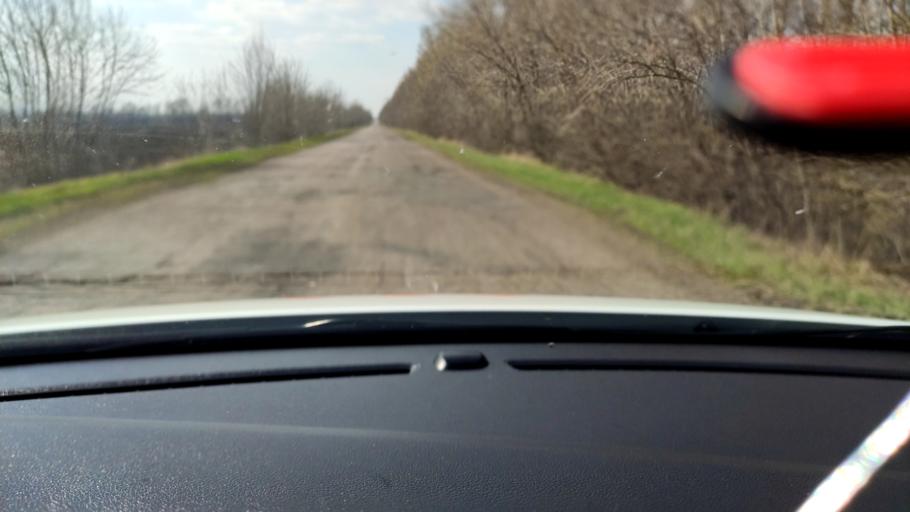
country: RU
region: Voronezj
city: Uryv-Pokrovka
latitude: 51.1319
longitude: 39.0978
